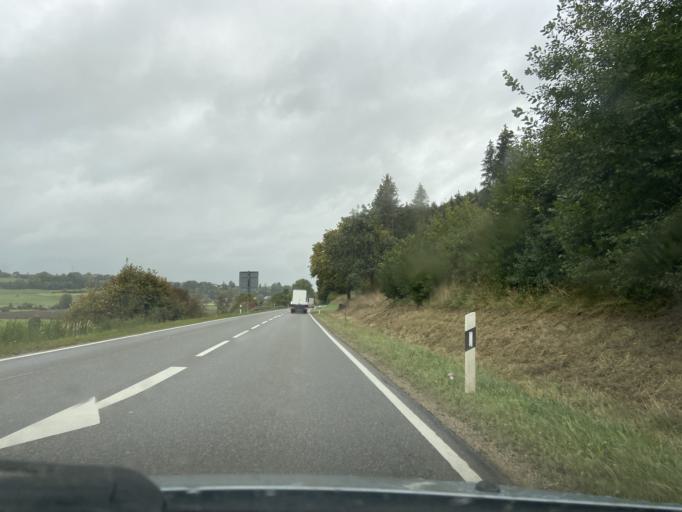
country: DE
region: Baden-Wuerttemberg
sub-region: Tuebingen Region
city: Krauchenwies
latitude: 48.0102
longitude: 9.2092
